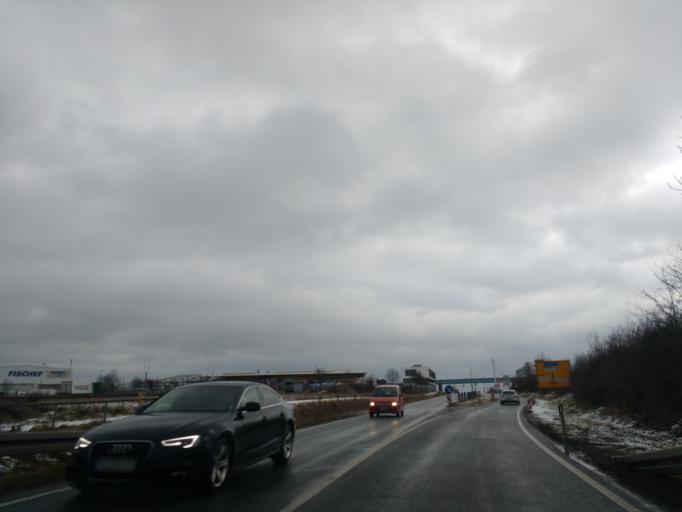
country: DE
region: Bavaria
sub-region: Regierungsbezirk Mittelfranken
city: Herzogenaurach
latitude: 49.5775
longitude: 10.8951
